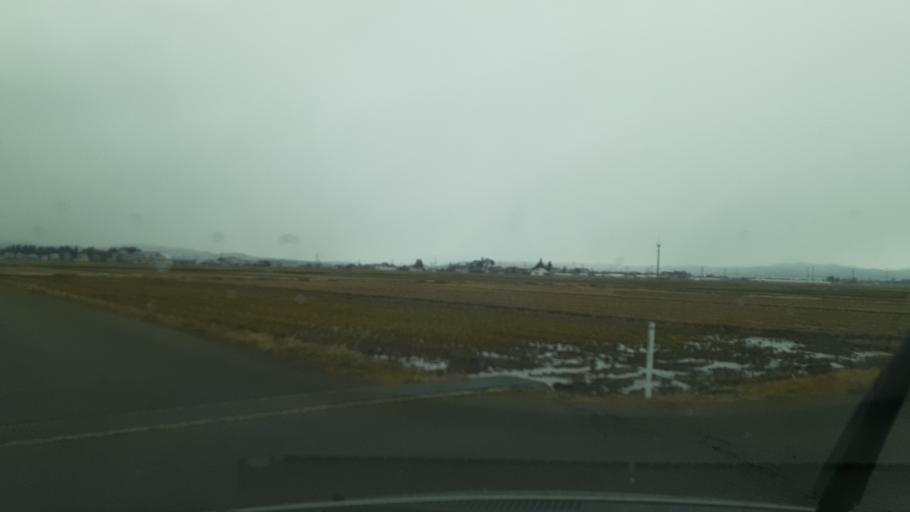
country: JP
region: Fukushima
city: Kitakata
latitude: 37.5596
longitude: 139.8830
